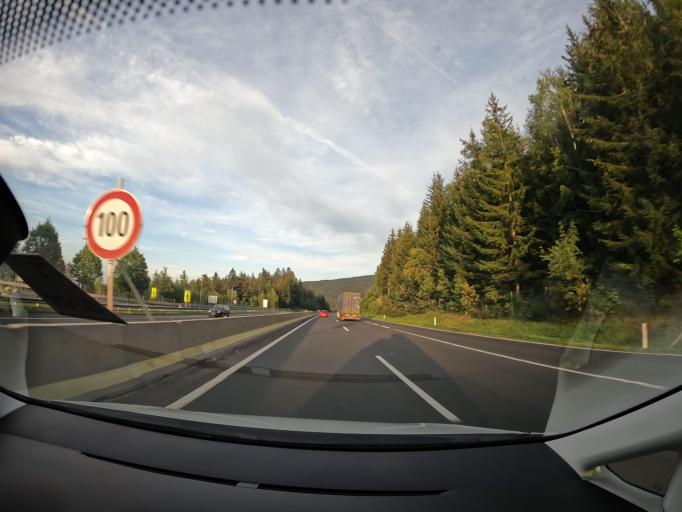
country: AT
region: Styria
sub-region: Politischer Bezirk Voitsberg
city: Voitsberg
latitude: 46.9899
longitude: 15.1133
